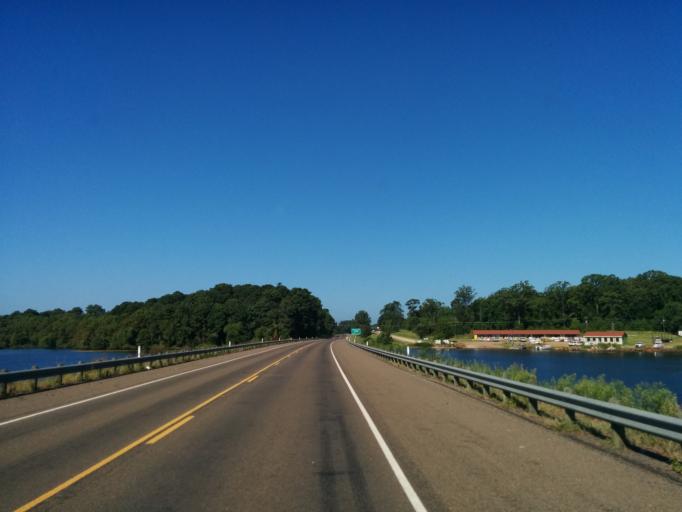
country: US
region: Texas
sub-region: Sabine County
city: Milam
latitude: 31.4641
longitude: -93.7490
